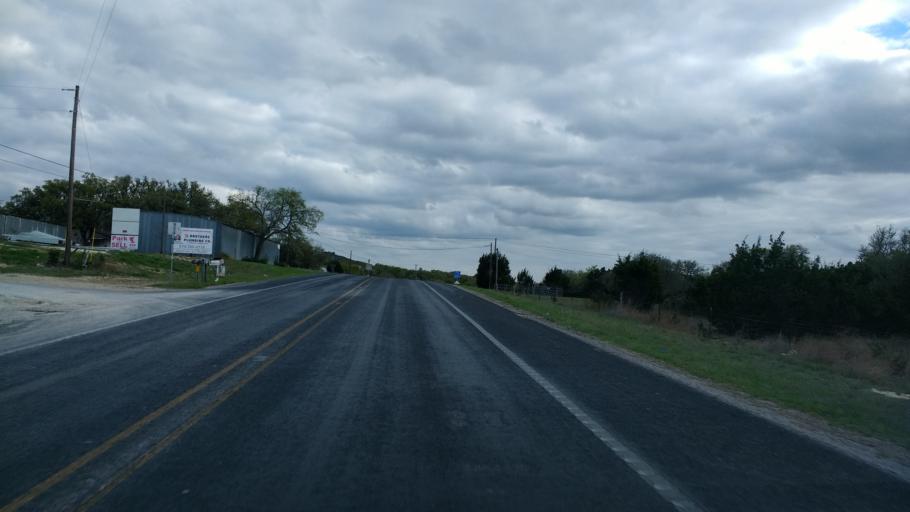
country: US
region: Texas
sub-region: Comal County
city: Canyon Lake
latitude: 29.9011
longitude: -98.2052
